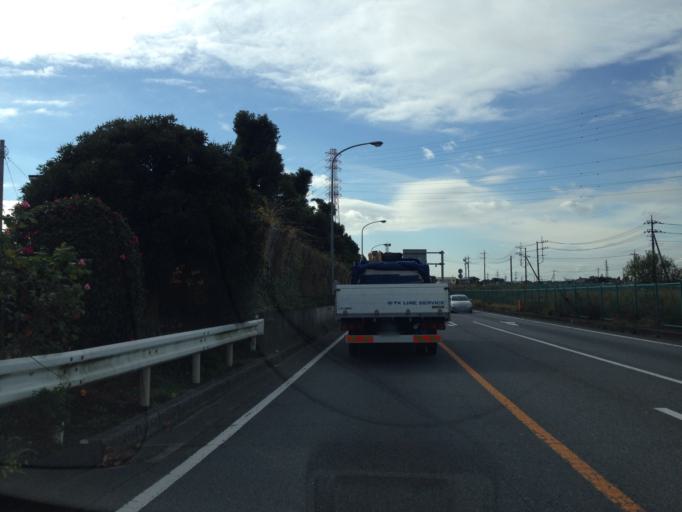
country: JP
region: Ibaraki
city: Fujishiro
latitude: 35.9244
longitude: 140.1080
